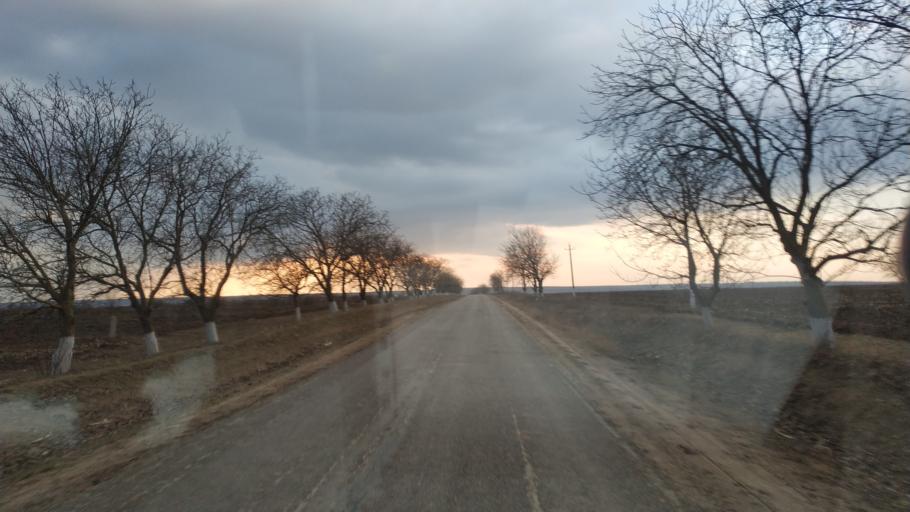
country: MD
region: Telenesti
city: Grigoriopol
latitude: 47.0249
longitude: 29.3343
